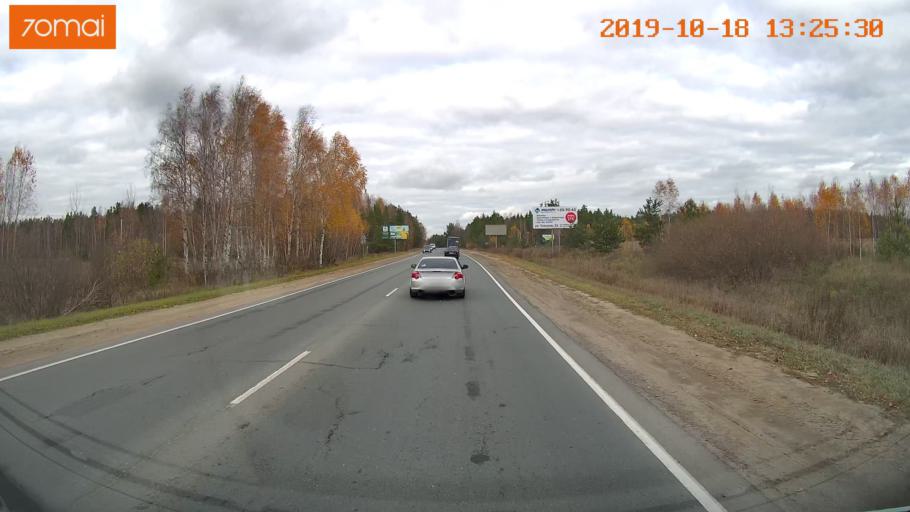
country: RU
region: Rjazan
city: Polyany
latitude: 54.7435
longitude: 39.8406
